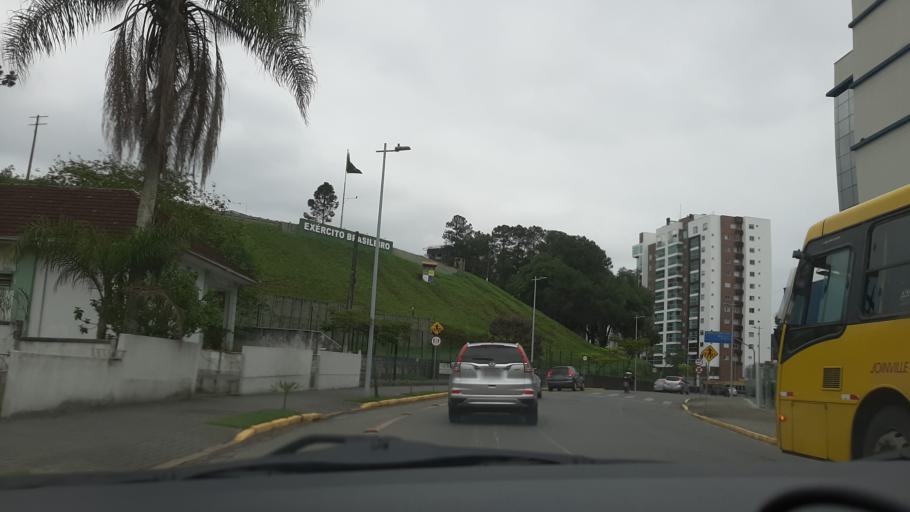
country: BR
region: Santa Catarina
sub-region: Joinville
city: Joinville
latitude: -26.3061
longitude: -48.8533
